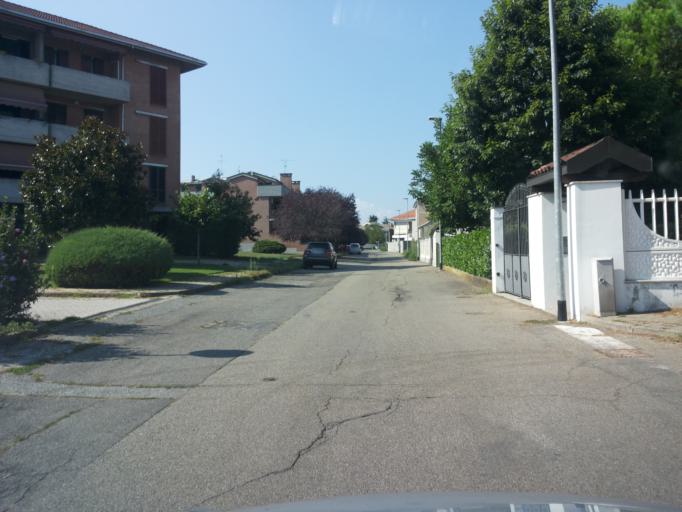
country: IT
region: Piedmont
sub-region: Provincia di Vercelli
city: Vercelli
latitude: 45.3133
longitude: 8.4310
